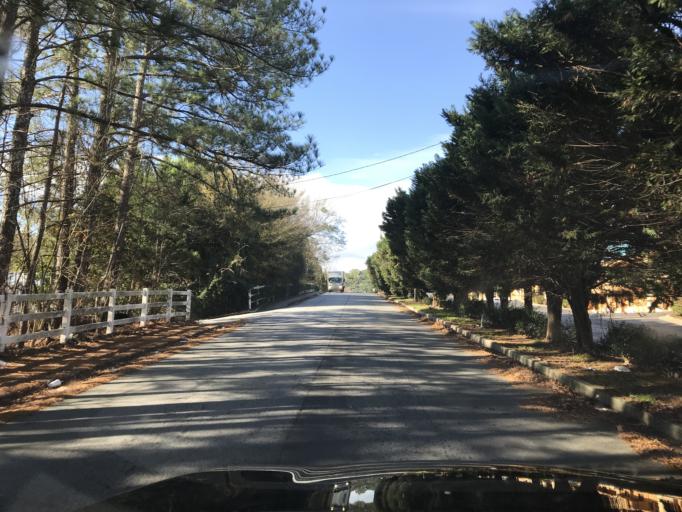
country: US
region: Georgia
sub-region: Clayton County
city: Forest Park
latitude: 33.5875
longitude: -84.3761
